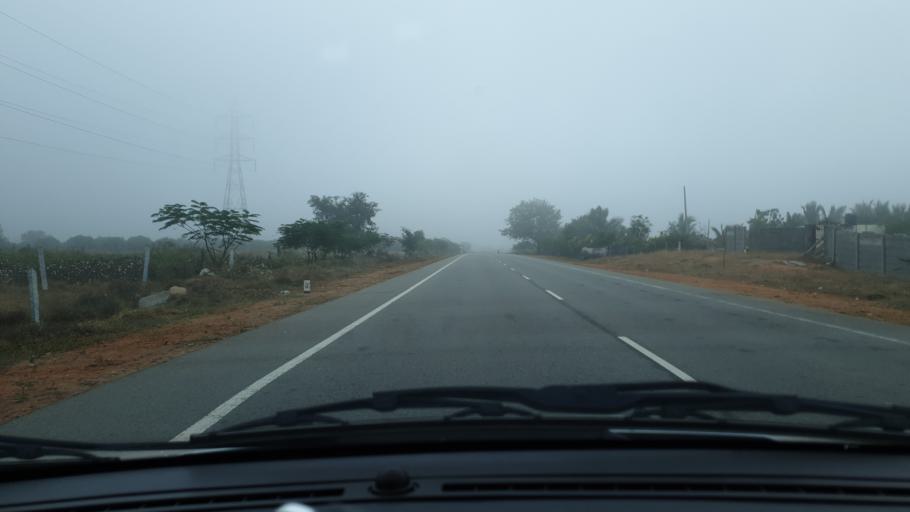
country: IN
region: Telangana
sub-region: Nalgonda
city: Devarkonda
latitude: 16.6246
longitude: 78.6686
